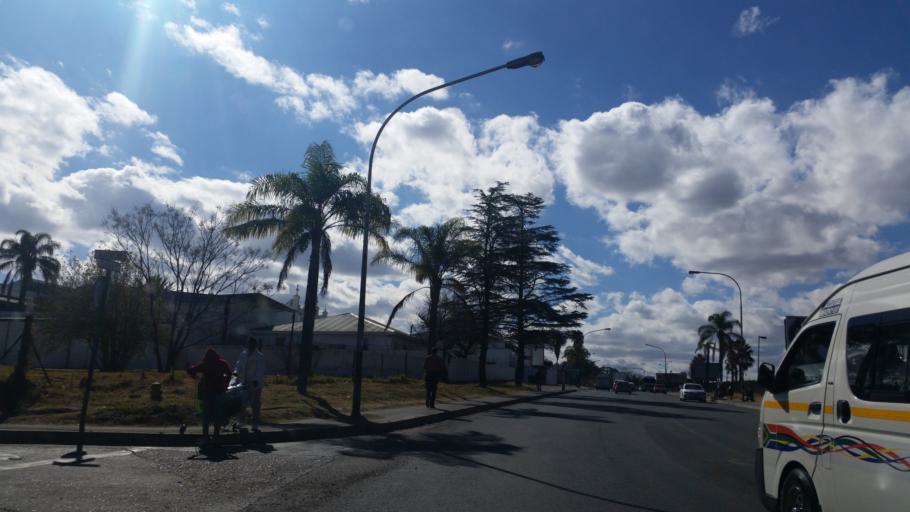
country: ZA
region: KwaZulu-Natal
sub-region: uThukela District Municipality
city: Ladysmith
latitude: -28.5556
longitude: 29.7852
